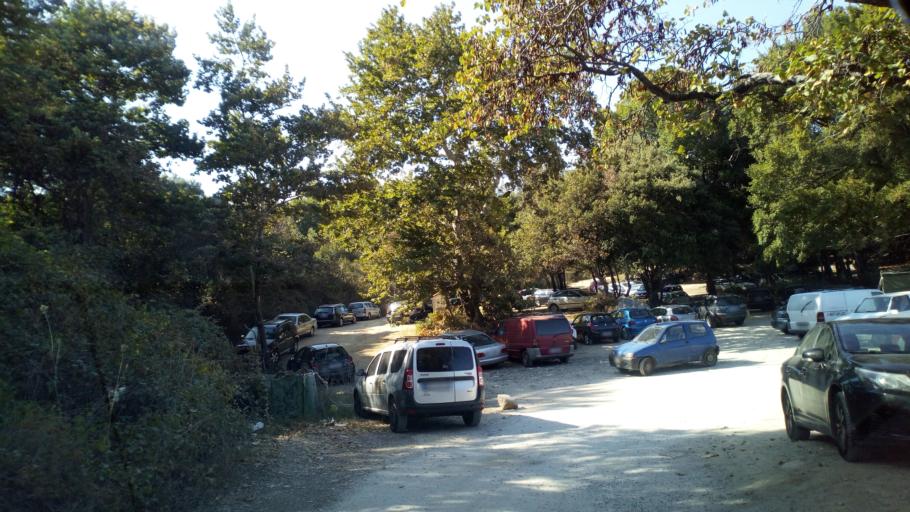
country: GR
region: Central Macedonia
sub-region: Nomos Chalkidikis
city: Stratonion
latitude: 40.5857
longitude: 23.7963
